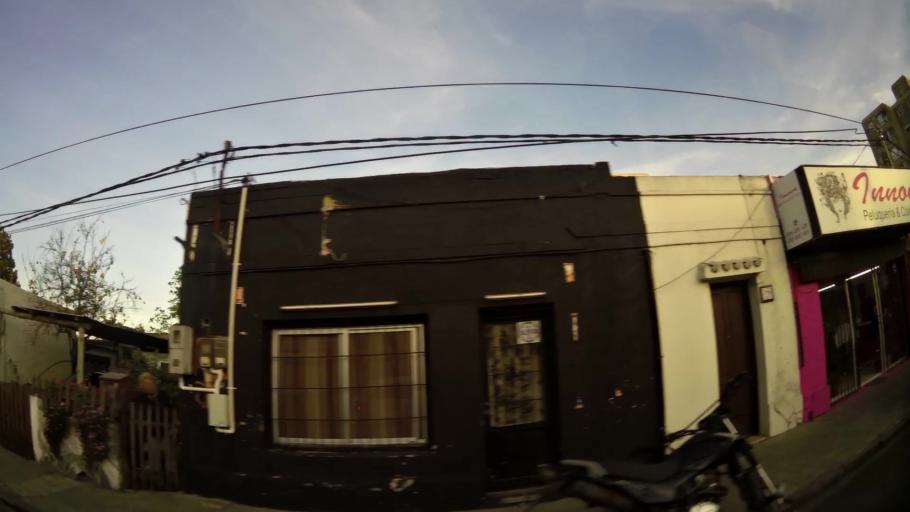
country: UY
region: Maldonado
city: Maldonado
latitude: -34.9096
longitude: -54.9533
